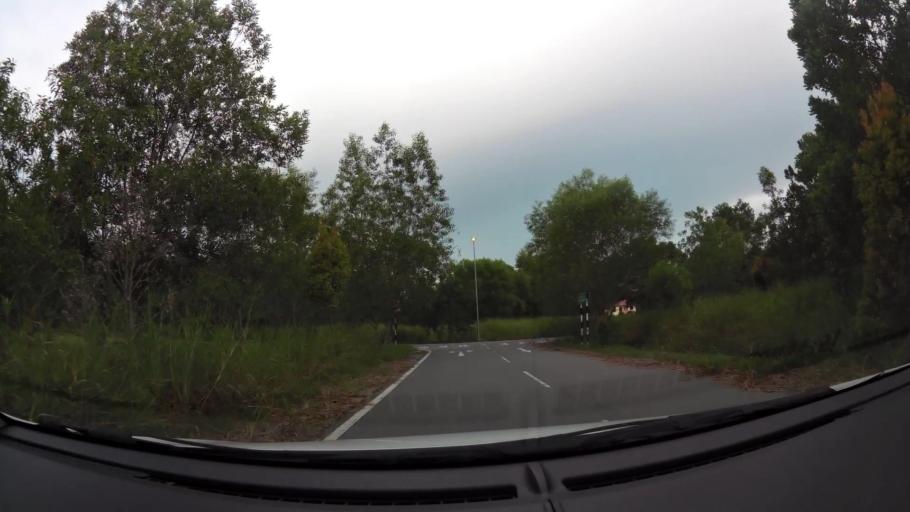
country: BN
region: Brunei and Muara
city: Bandar Seri Begawan
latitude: 4.9944
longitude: 114.9898
